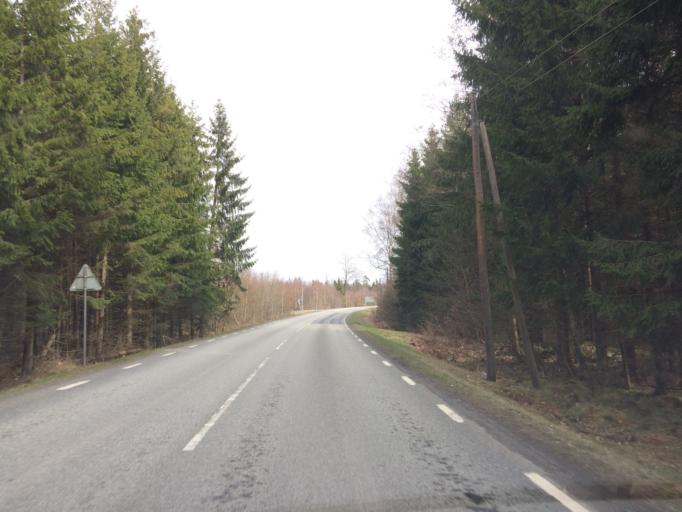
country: SE
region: Skane
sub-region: Osby Kommun
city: Lonsboda
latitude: 56.4040
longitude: 14.3309
